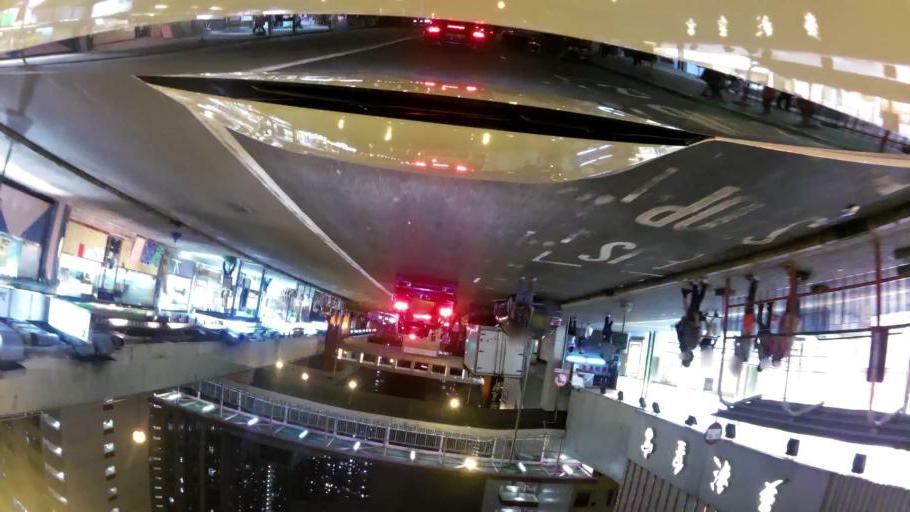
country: HK
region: Sham Shui Po
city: Sham Shui Po
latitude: 22.3326
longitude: 114.1663
